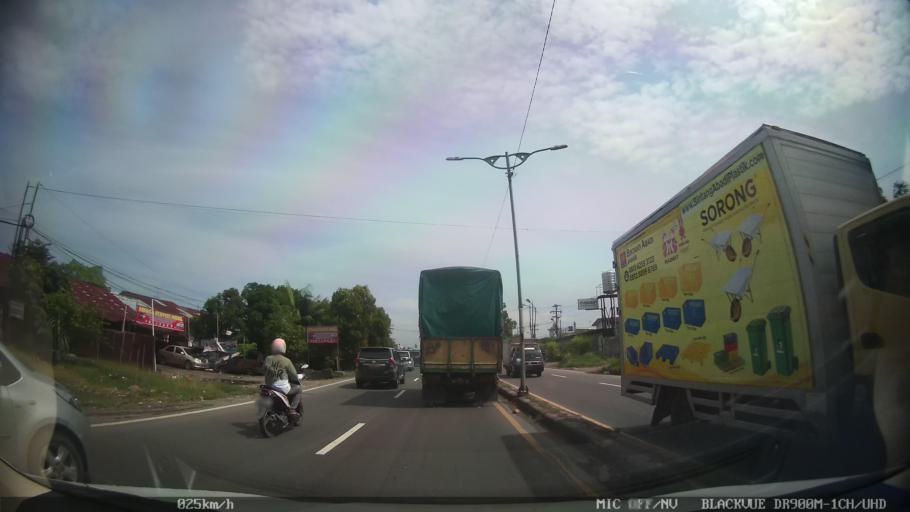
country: ID
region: North Sumatra
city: Sunggal
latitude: 3.6097
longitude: 98.6276
